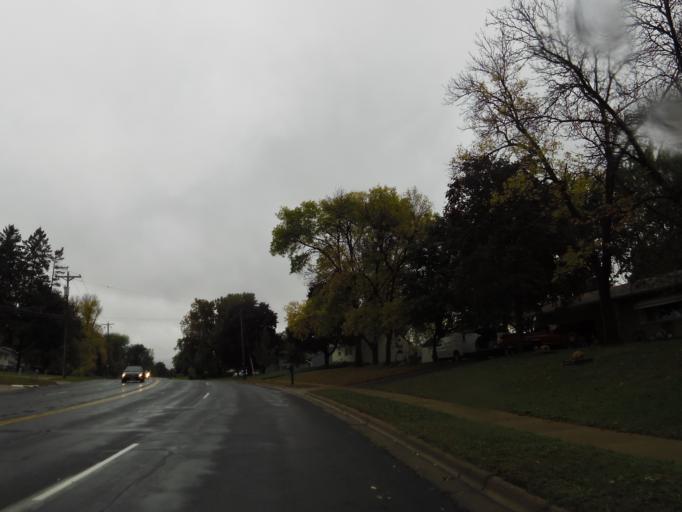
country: US
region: Minnesota
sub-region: Dakota County
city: Inver Grove Heights
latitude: 44.8419
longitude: -93.0404
